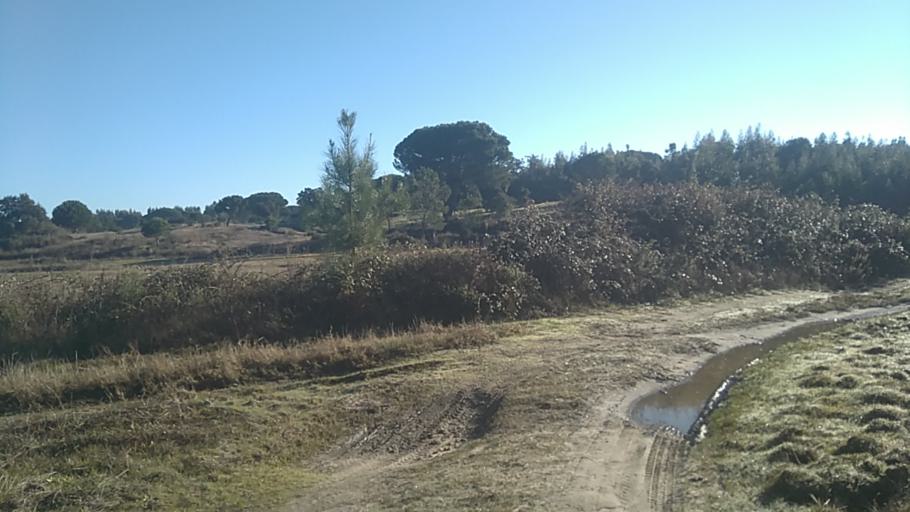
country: PT
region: Santarem
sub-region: Coruche
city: Coruche
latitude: 38.8657
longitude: -8.5191
